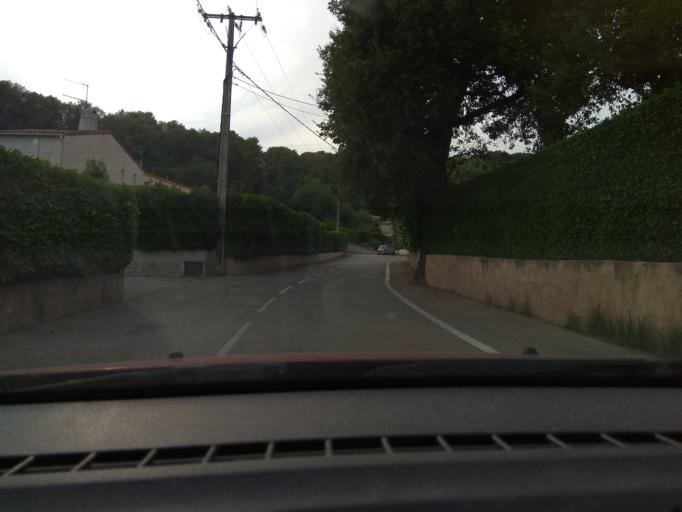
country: FR
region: Provence-Alpes-Cote d'Azur
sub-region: Departement des Alpes-Maritimes
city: La Colle-sur-Loup
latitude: 43.6743
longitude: 7.1074
